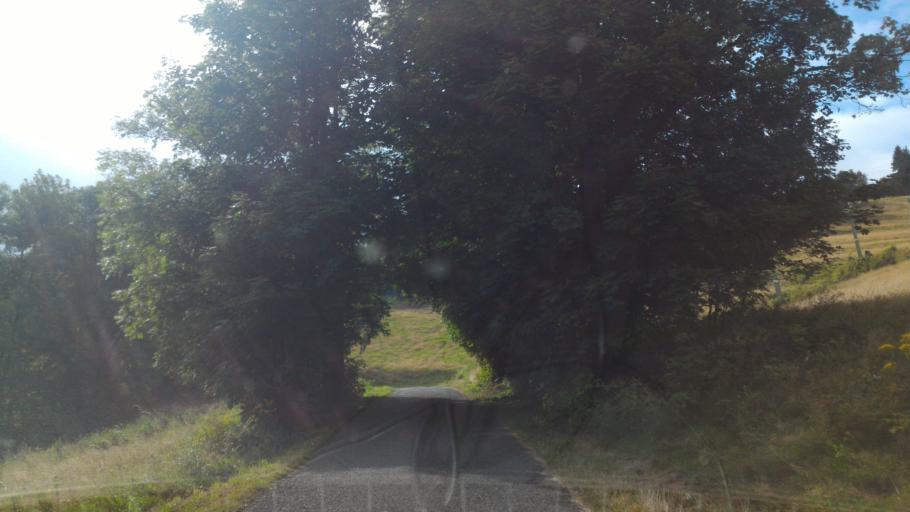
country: CZ
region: Ustecky
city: Dolni Podluzi
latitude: 50.8596
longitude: 14.5770
